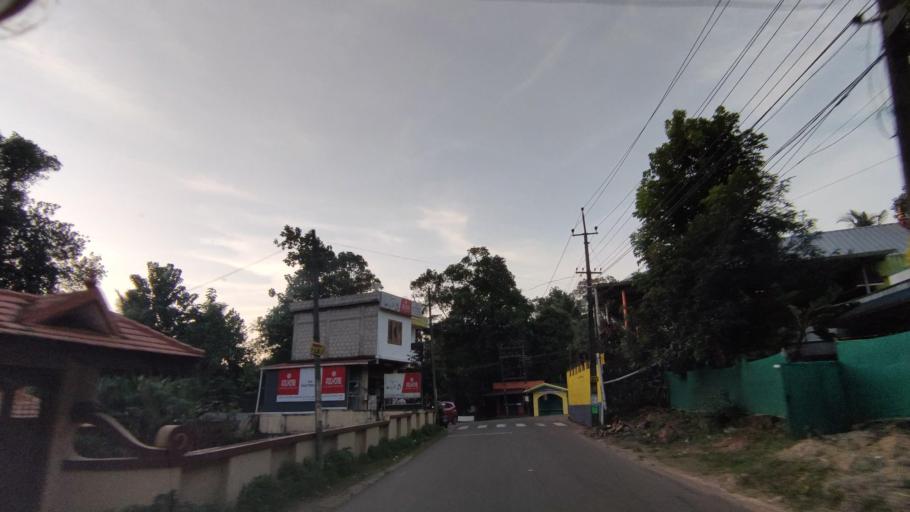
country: IN
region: Kerala
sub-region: Kottayam
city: Kottayam
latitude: 9.6523
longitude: 76.5088
